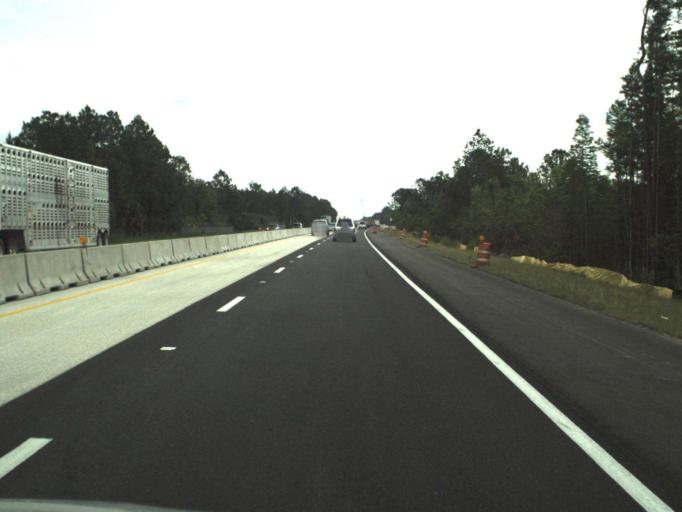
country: US
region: Florida
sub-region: Volusia County
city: Lake Helen
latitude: 29.0650
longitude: -81.1872
